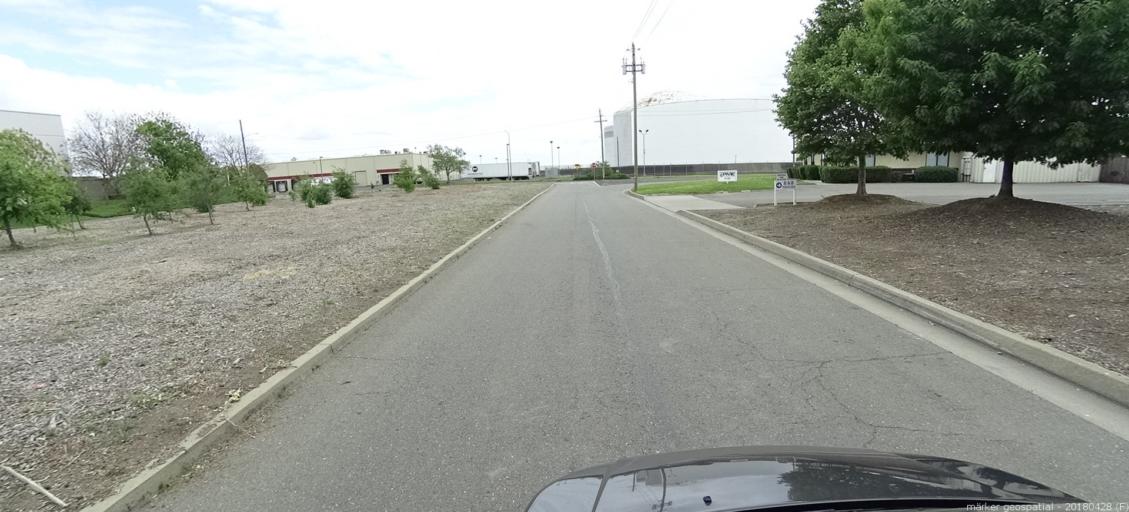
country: US
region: California
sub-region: Yolo County
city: West Sacramento
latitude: 38.5604
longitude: -121.5760
